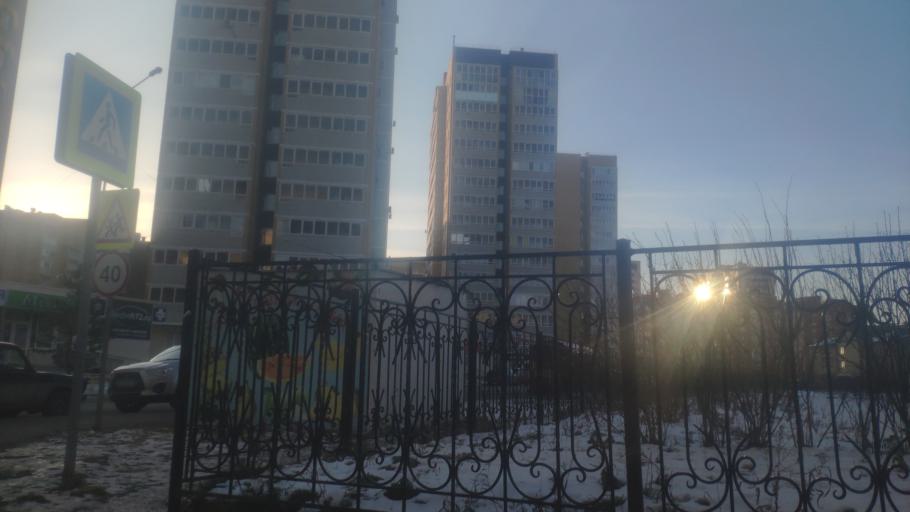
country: RU
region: Tjumen
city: Tyumen
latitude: 57.1769
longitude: 65.5661
